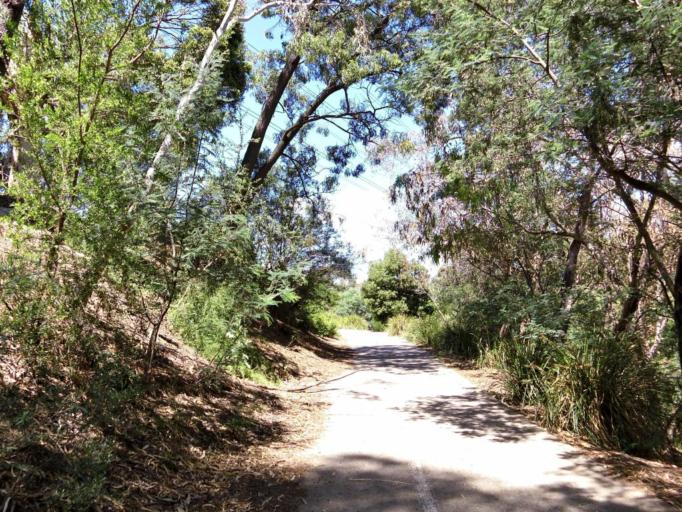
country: AU
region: Victoria
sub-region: Moreland
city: Coburg
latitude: -37.7480
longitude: 144.9811
